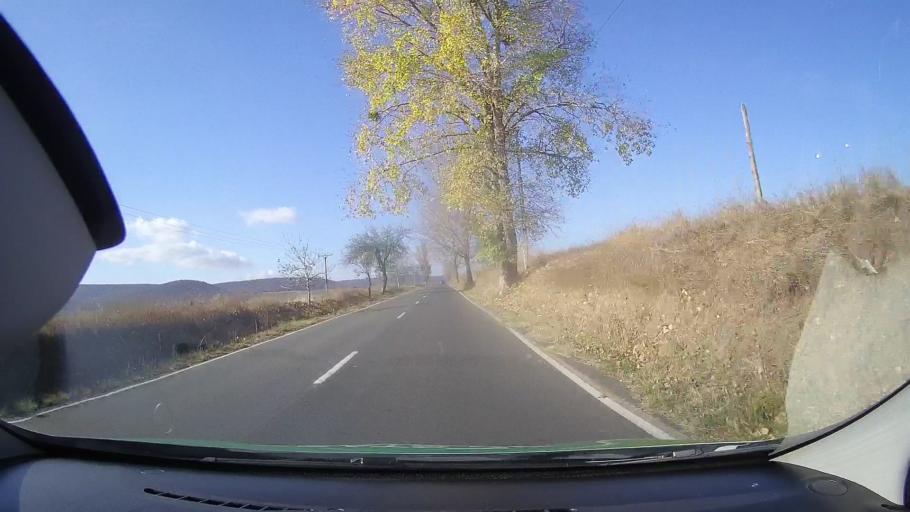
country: RO
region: Tulcea
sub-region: Comuna Sarichioi
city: Enisala
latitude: 44.8793
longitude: 28.7854
